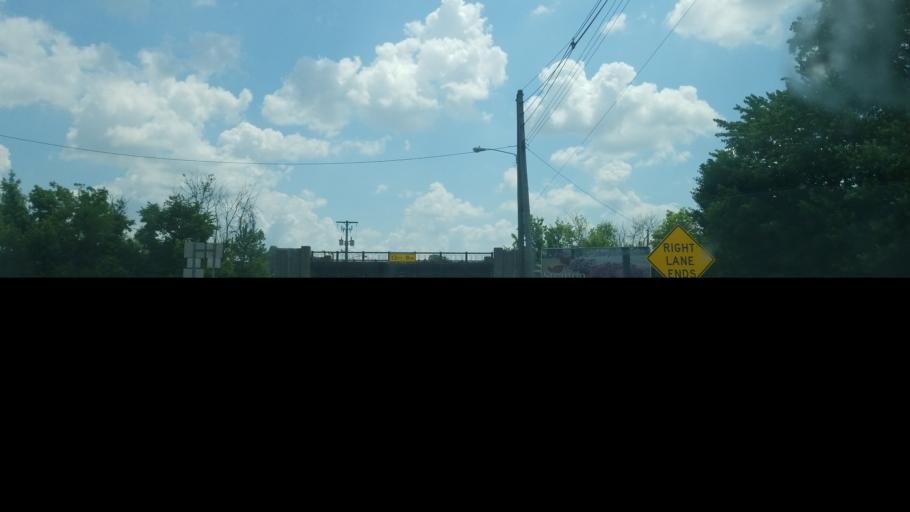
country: US
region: Ohio
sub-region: Allen County
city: Lima
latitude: 40.7372
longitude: -84.1018
